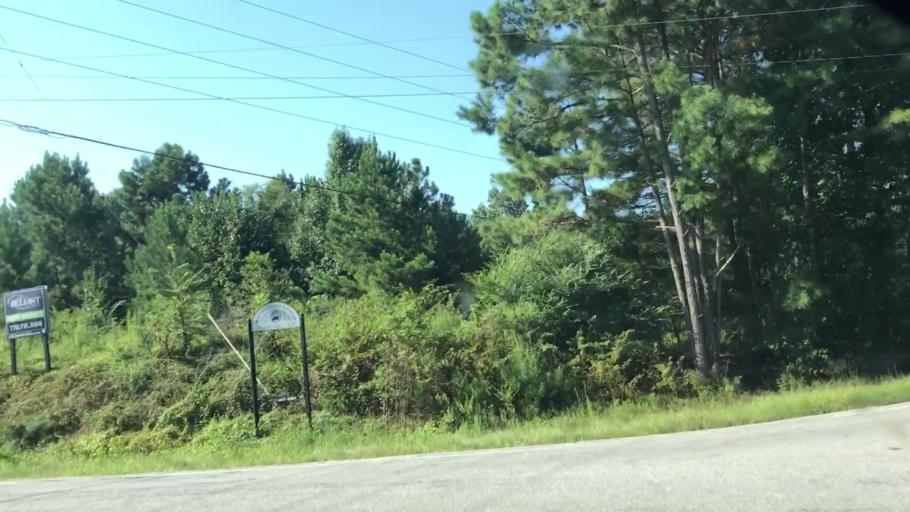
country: US
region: Georgia
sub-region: Walton County
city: Loganville
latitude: 33.8856
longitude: -83.8121
